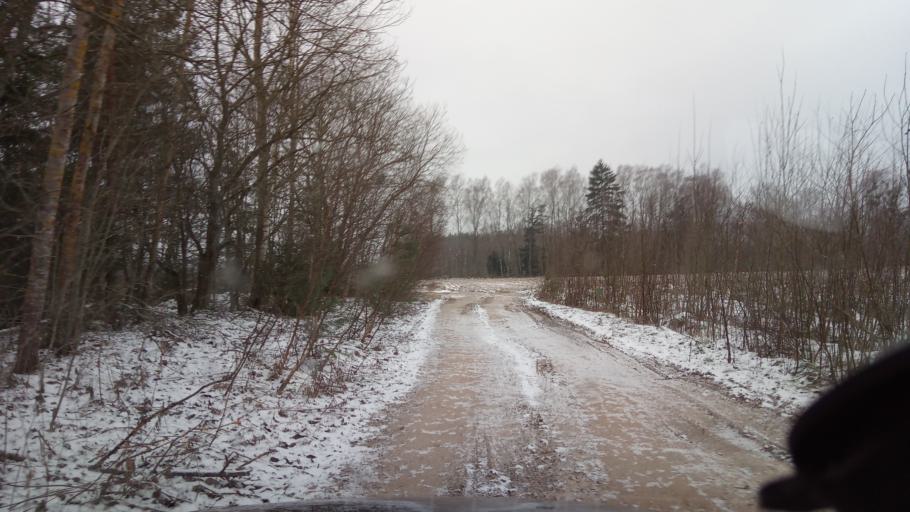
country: LT
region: Alytaus apskritis
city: Varena
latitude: 54.1372
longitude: 24.6986
